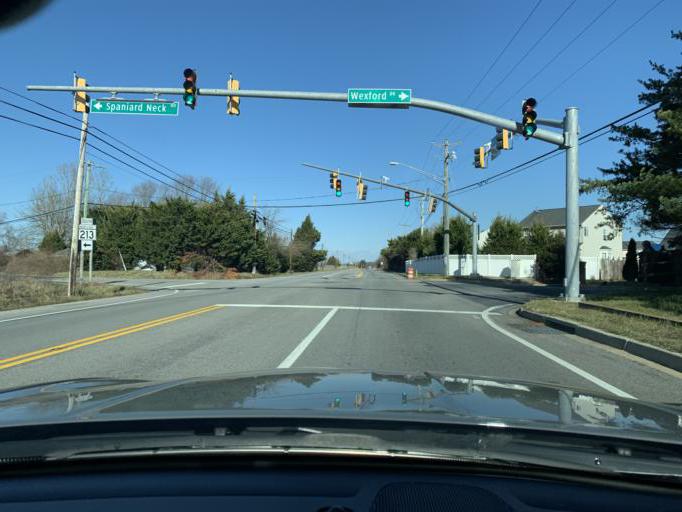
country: US
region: Maryland
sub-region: Queen Anne's County
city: Centreville
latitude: 39.0598
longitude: -76.0528
